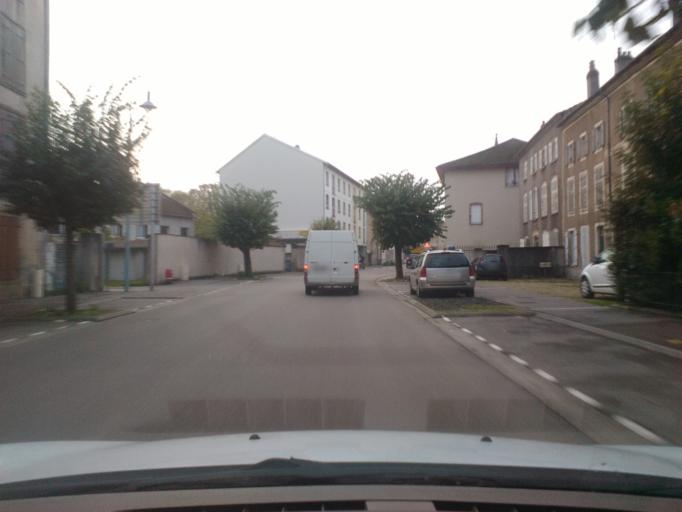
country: FR
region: Lorraine
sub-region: Departement des Vosges
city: Mirecourt
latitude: 48.3070
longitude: 6.1339
